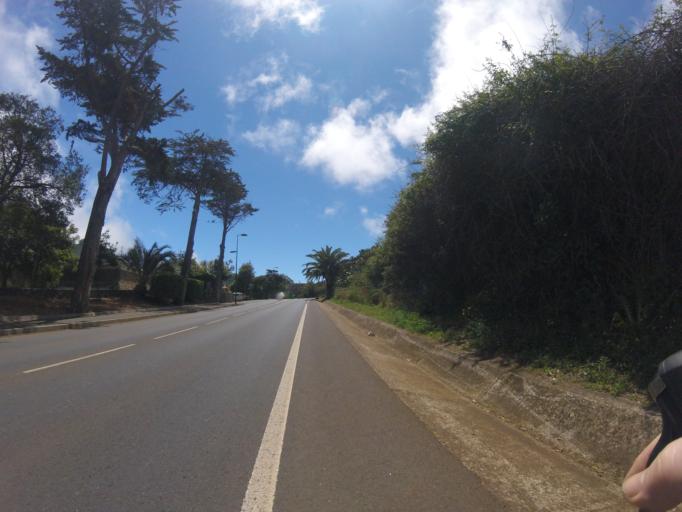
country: ES
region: Canary Islands
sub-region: Provincia de Santa Cruz de Tenerife
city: Tegueste
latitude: 28.5192
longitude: -16.3323
